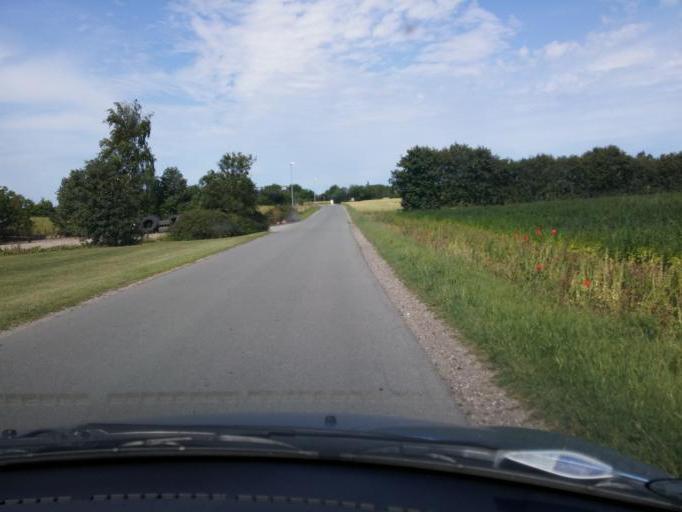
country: DK
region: South Denmark
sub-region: Kerteminde Kommune
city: Langeskov
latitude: 55.4077
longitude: 10.6006
